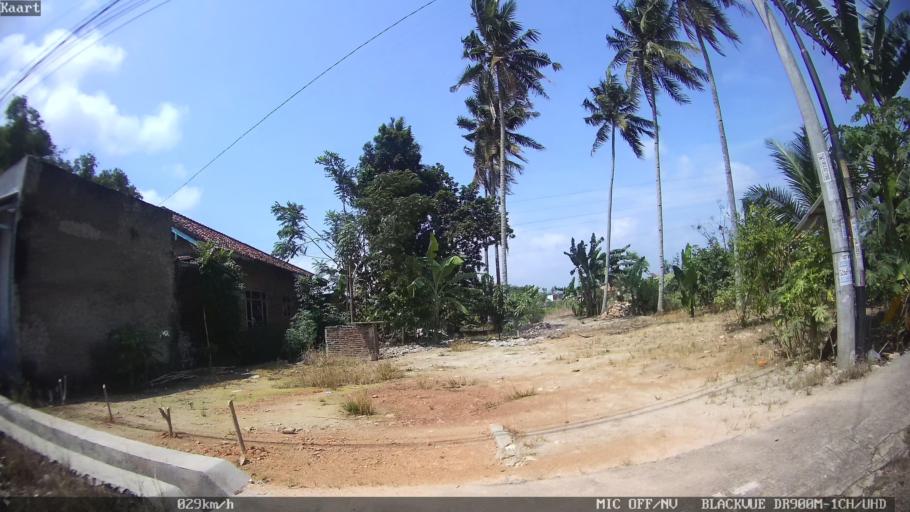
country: ID
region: Lampung
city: Kedaton
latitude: -5.3487
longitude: 105.2800
